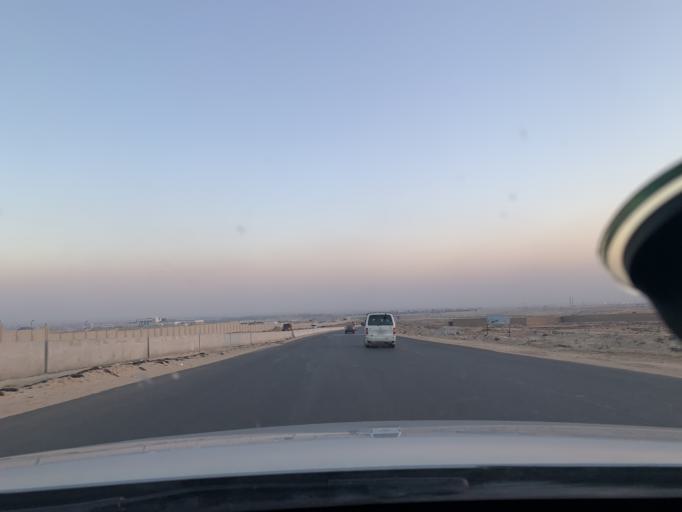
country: EG
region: Muhafazat al Qalyubiyah
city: Al Khankah
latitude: 30.2237
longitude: 31.4266
